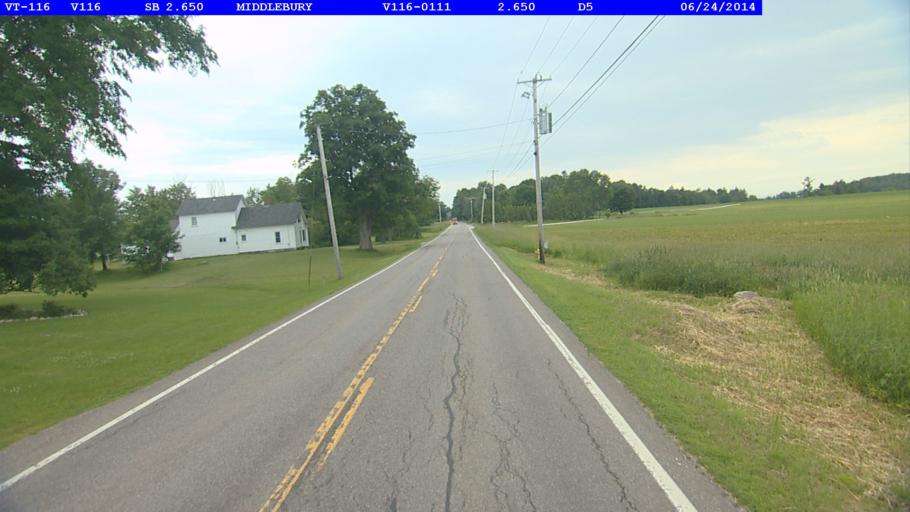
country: US
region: Vermont
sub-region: Addison County
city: Middlebury (village)
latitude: 44.0021
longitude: -73.1004
